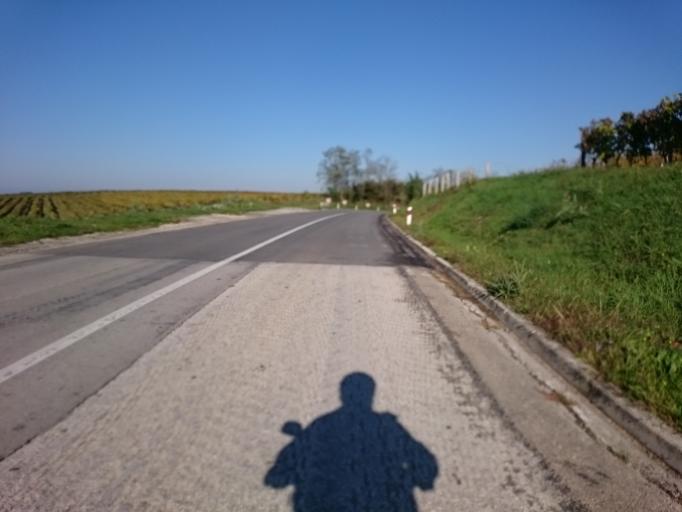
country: HR
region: Istarska
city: Buje
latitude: 45.3997
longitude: 13.6392
